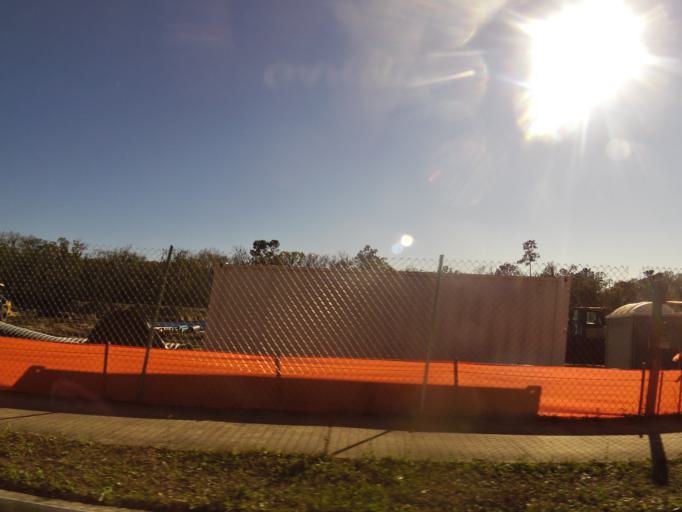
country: US
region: Florida
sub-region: Duval County
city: Jacksonville
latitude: 30.2477
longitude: -81.5697
